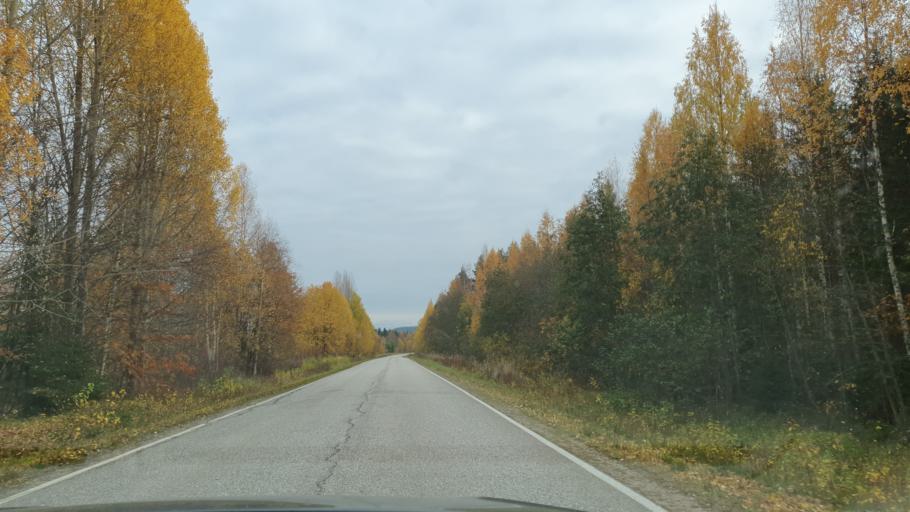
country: FI
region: Kainuu
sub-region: Kajaani
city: Ristijaervi
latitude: 64.4694
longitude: 28.3003
